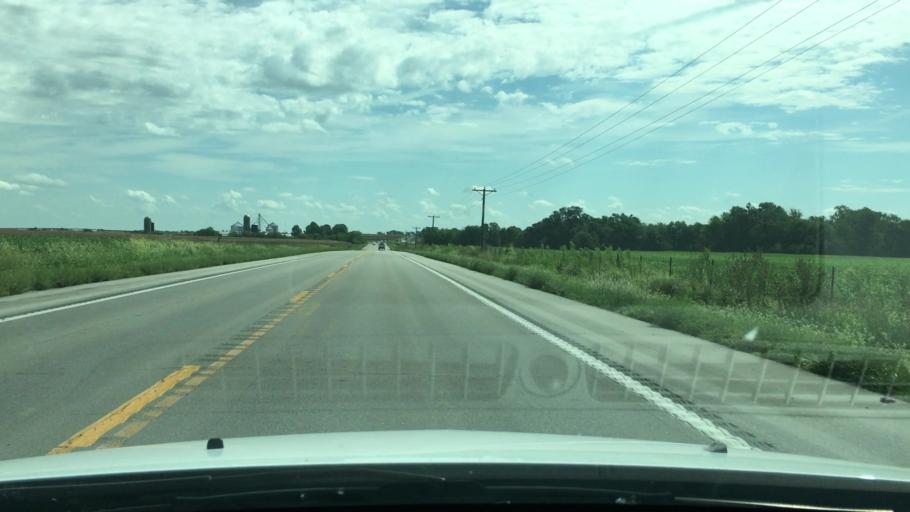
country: US
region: Missouri
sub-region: Montgomery County
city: Wellsville
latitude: 39.1644
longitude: -91.7122
